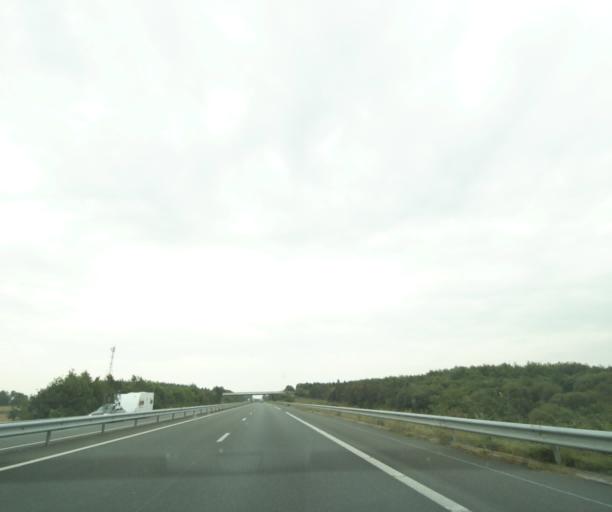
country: FR
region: Pays de la Loire
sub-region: Departement de la Vendee
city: Saint-Martin-des-Noyers
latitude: 46.6875
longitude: -1.1568
